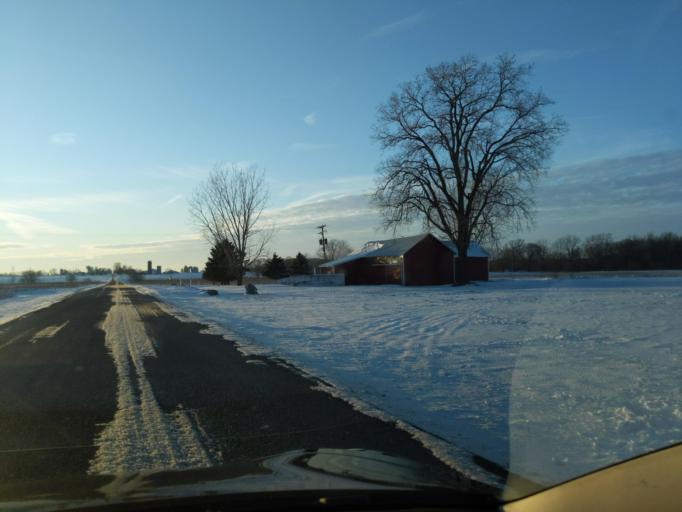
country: US
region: Michigan
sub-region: Ingham County
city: Webberville
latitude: 42.5692
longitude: -84.1765
